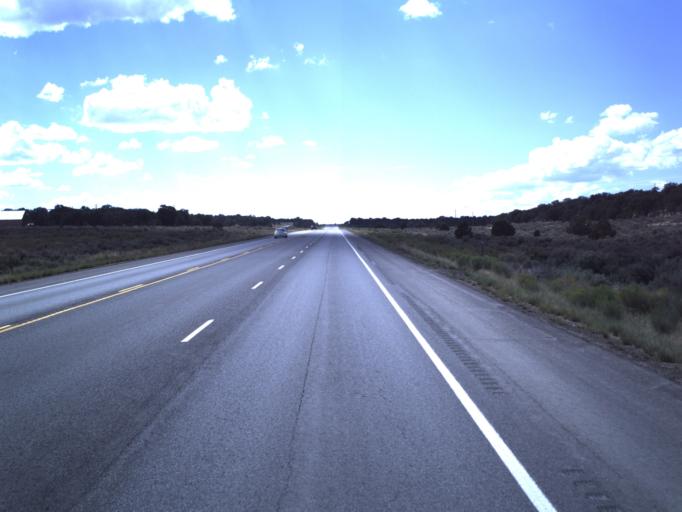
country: US
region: Utah
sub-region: Duchesne County
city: Duchesne
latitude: 40.1804
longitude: -110.6188
